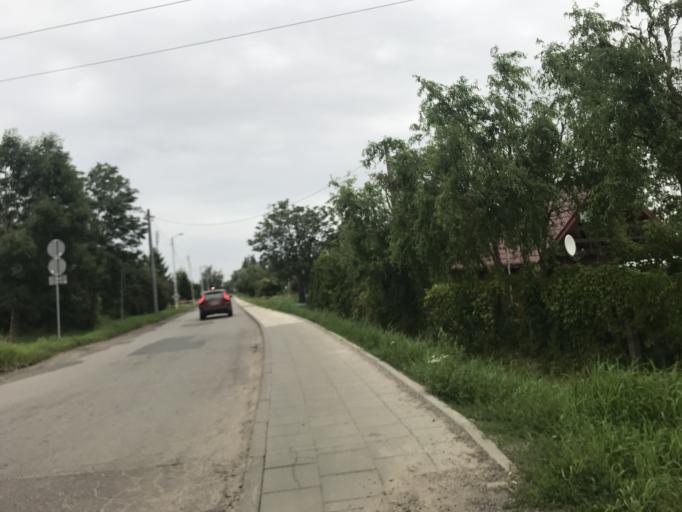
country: PL
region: Pomeranian Voivodeship
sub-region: Gdansk
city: Gdansk
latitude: 54.3459
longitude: 18.6802
